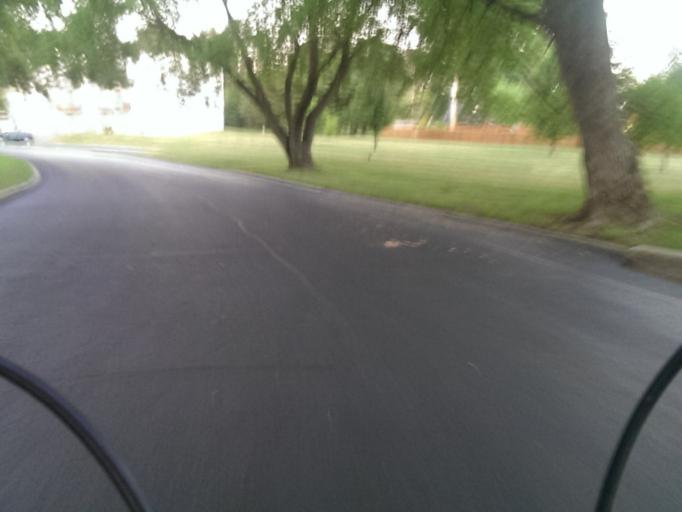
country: US
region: Missouri
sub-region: Jackson County
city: Grandview
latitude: 38.9141
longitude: -94.5779
